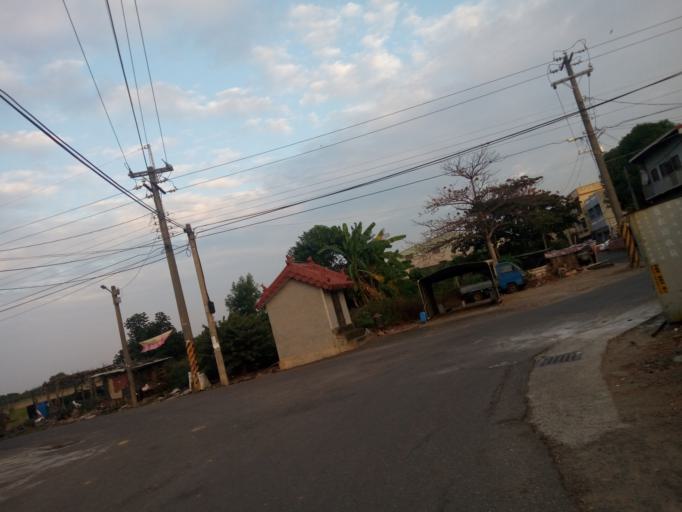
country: TW
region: Taiwan
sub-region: Chiayi
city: Jiayi Shi
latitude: 23.5001
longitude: 120.3854
